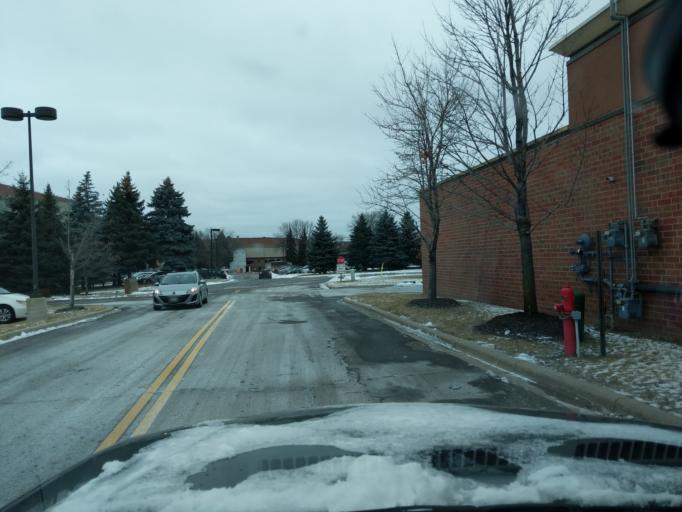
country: US
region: Minnesota
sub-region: Hennepin County
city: Eden Prairie
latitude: 44.8512
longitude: -93.4344
